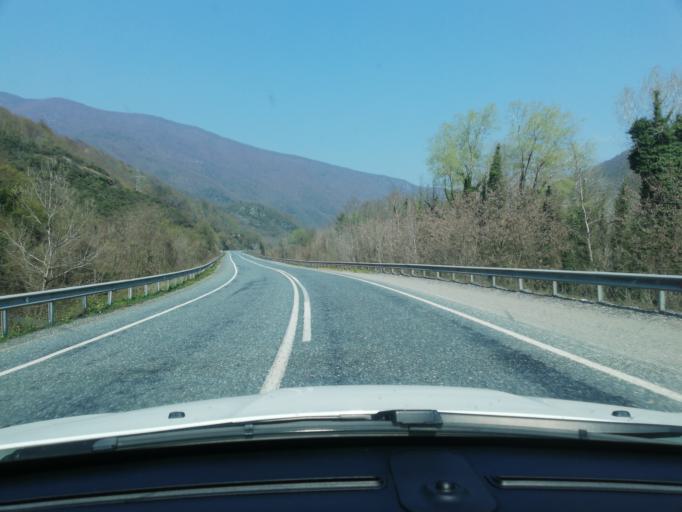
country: TR
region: Zonguldak
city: Gokcebey
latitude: 41.2528
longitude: 32.1624
